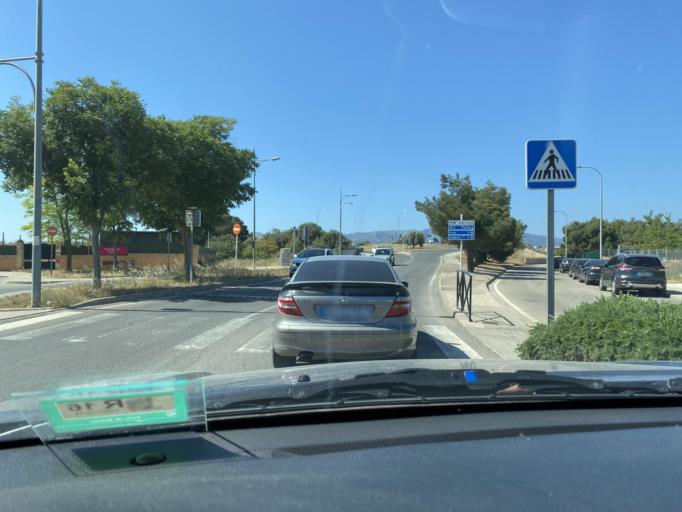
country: ES
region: Balearic Islands
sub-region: Illes Balears
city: Palma
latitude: 39.6046
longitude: 2.6864
